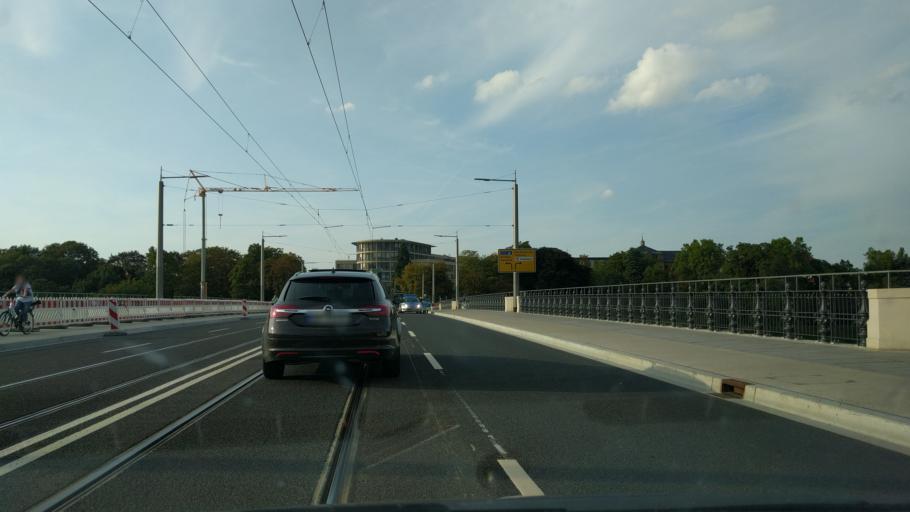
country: DE
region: Saxony
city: Dresden
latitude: 51.0571
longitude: 13.7547
